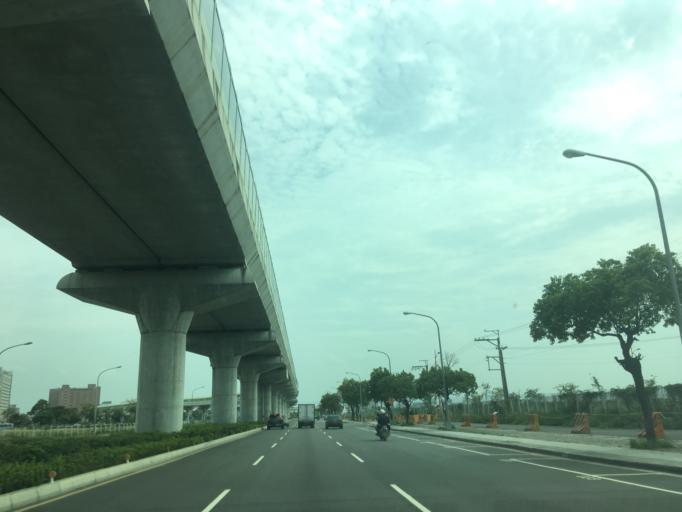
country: TW
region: Taiwan
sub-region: Taichung City
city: Taichung
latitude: 24.1289
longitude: 120.6463
